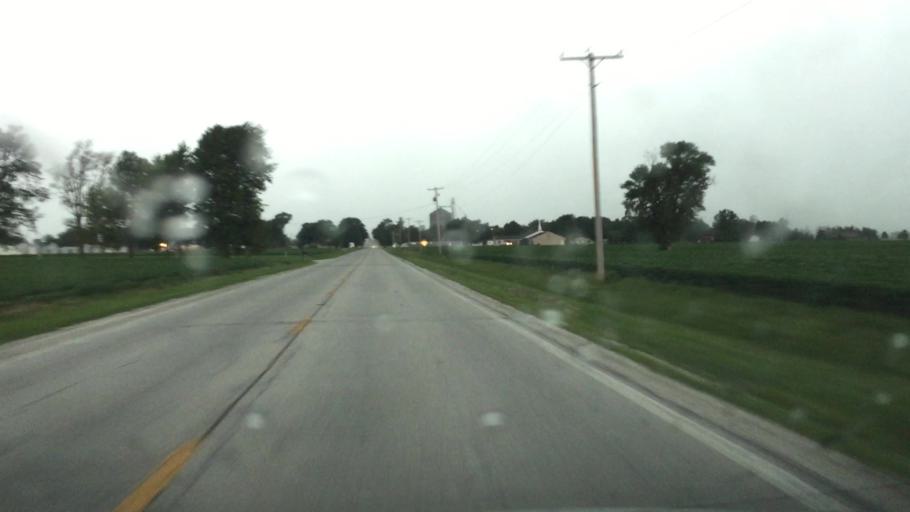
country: US
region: Illinois
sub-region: Adams County
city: Camp Point
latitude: 40.2314
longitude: -91.0512
